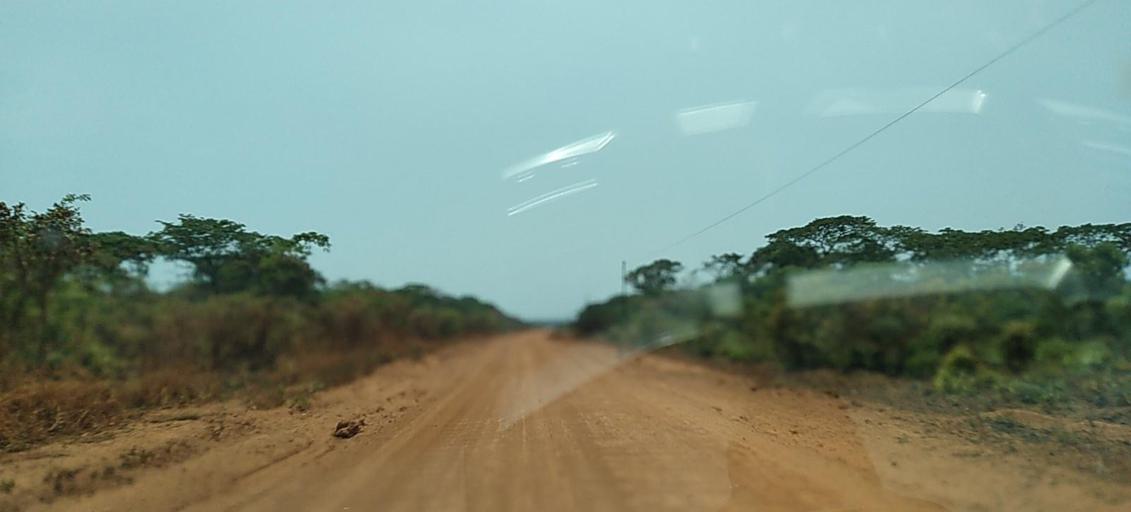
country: CD
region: Katanga
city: Kipushi
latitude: -11.9407
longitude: 26.9454
